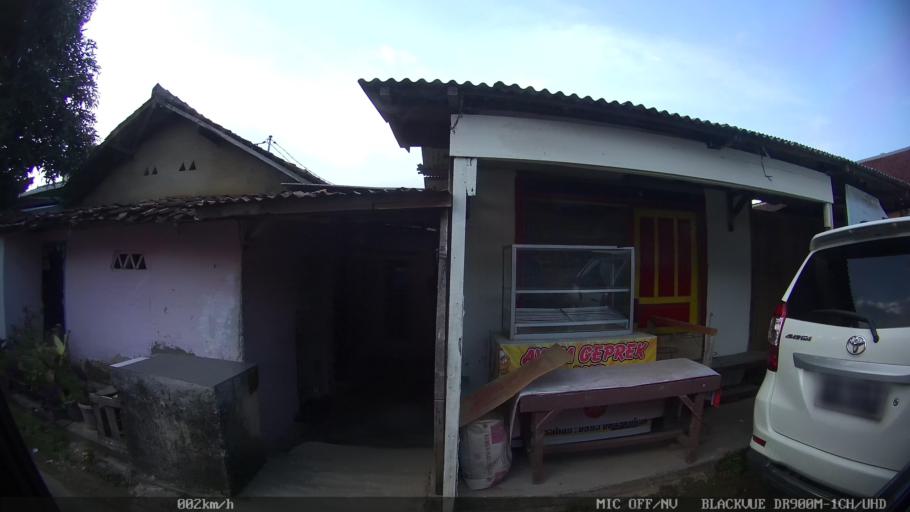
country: ID
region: Lampung
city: Kedaton
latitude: -5.3916
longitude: 105.2656
